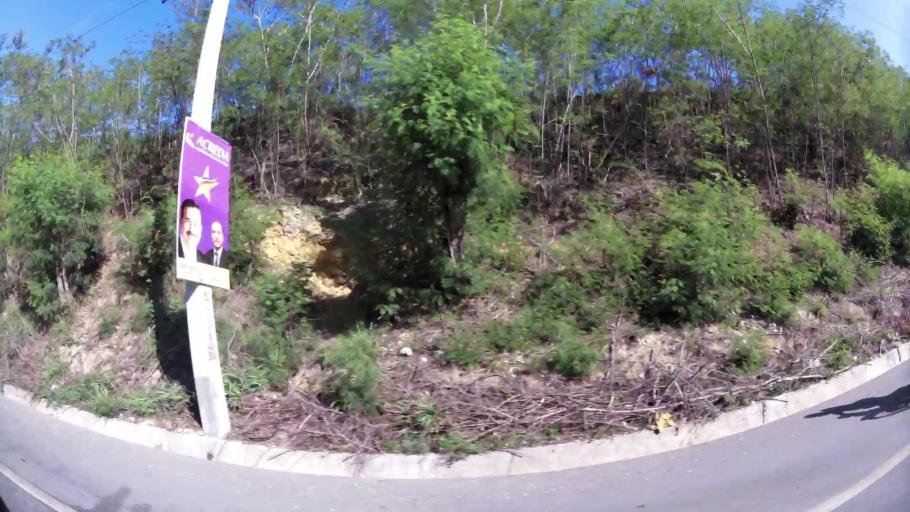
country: DO
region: San Cristobal
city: Bajos de Haina
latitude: 18.4324
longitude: -70.0387
